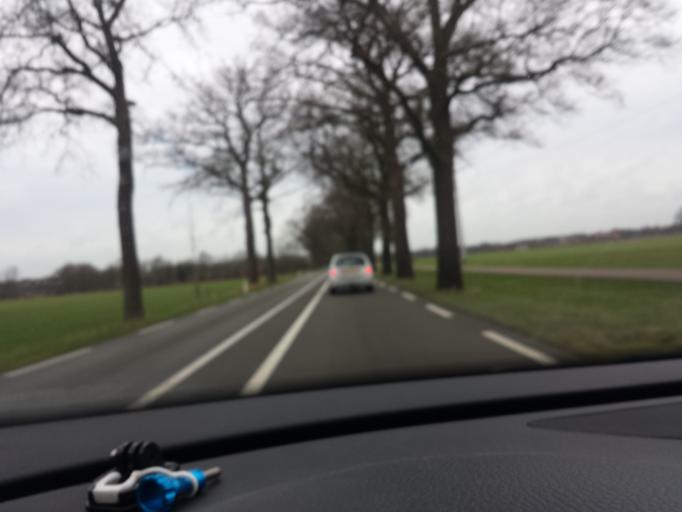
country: NL
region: Gelderland
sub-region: Oost Gelre
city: Lichtenvoorde
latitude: 52.0207
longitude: 6.6373
